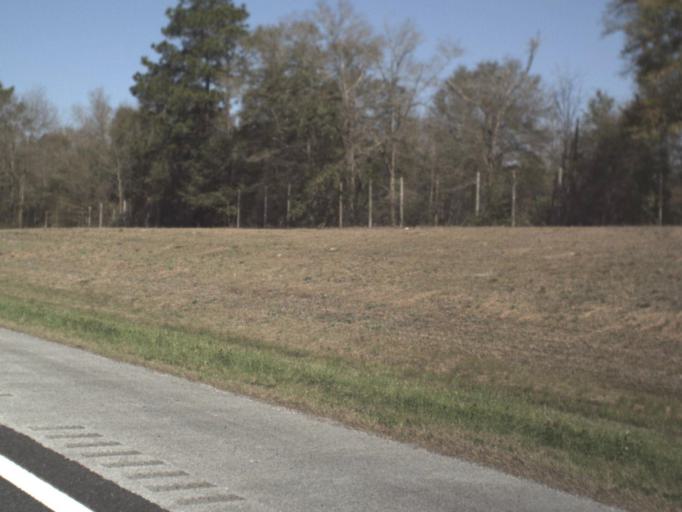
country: US
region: Florida
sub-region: Jackson County
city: Sneads
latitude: 30.6677
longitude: -85.0571
